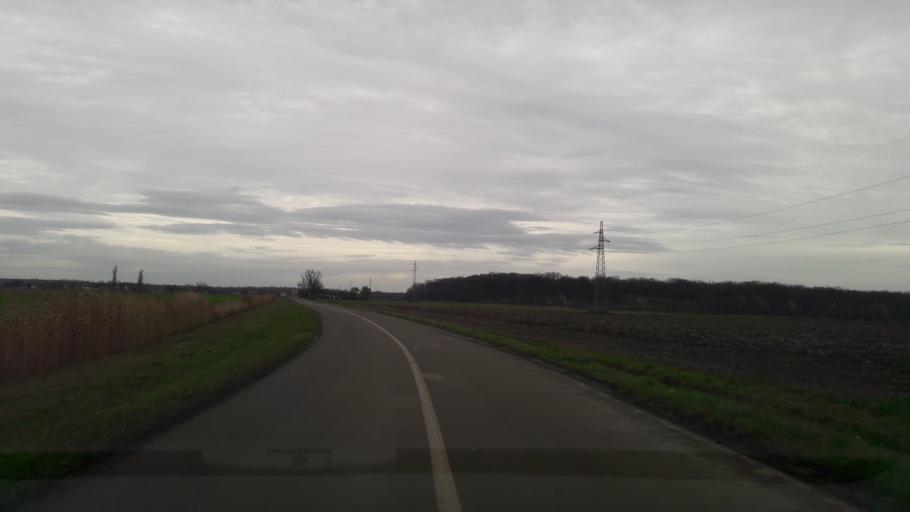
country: HR
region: Osjecko-Baranjska
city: Velimirovac
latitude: 45.6096
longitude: 18.0613
